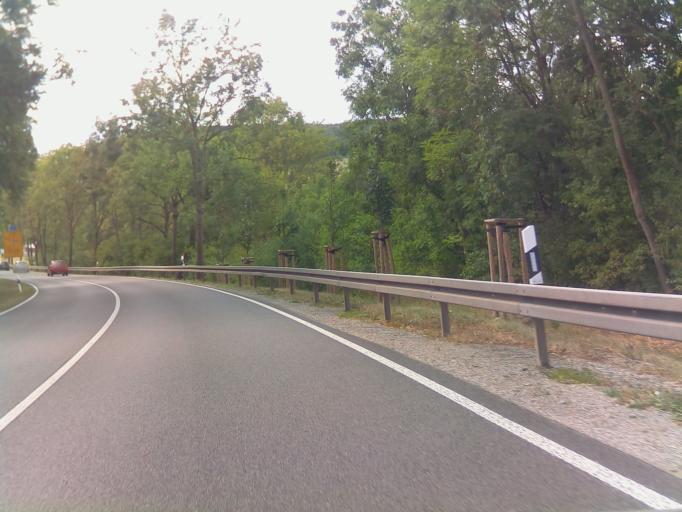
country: DE
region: Thuringia
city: Obermassfeld-Grimmenthal
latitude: 50.5233
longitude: 10.4386
